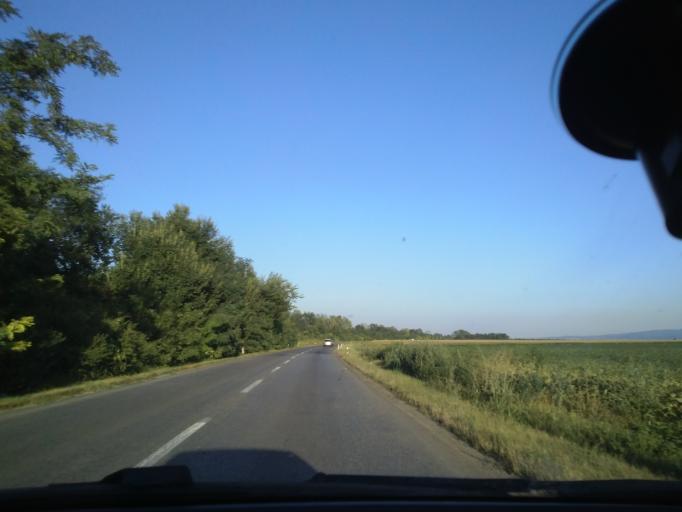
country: RS
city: Kisac
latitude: 45.3337
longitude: 19.6782
